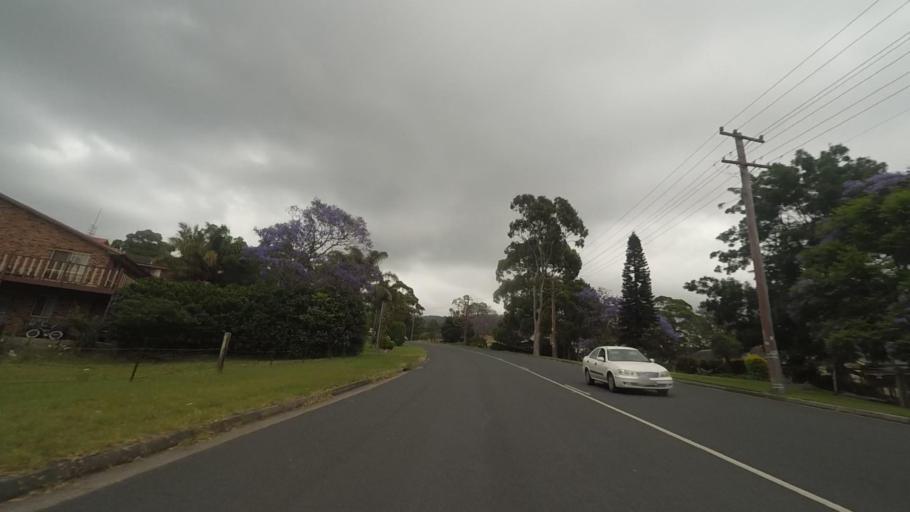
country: AU
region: New South Wales
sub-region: Wollongong
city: Cordeaux Heights
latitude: -34.4309
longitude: 150.8280
